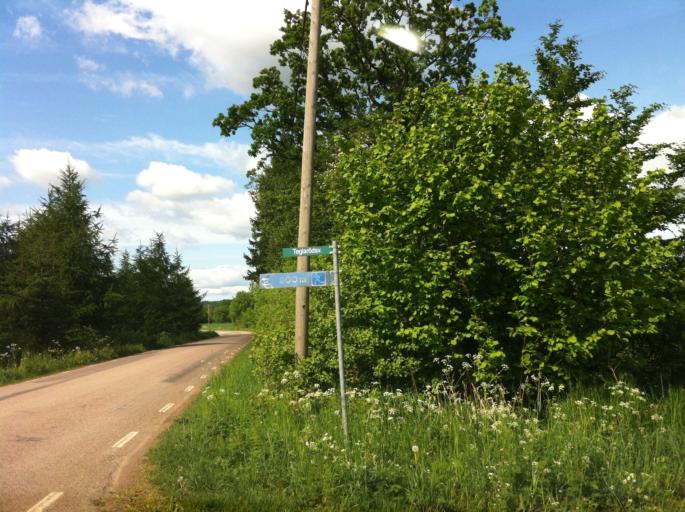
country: SE
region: Skane
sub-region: Svalovs Kommun
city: Kagerod
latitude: 55.9648
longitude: 13.0468
